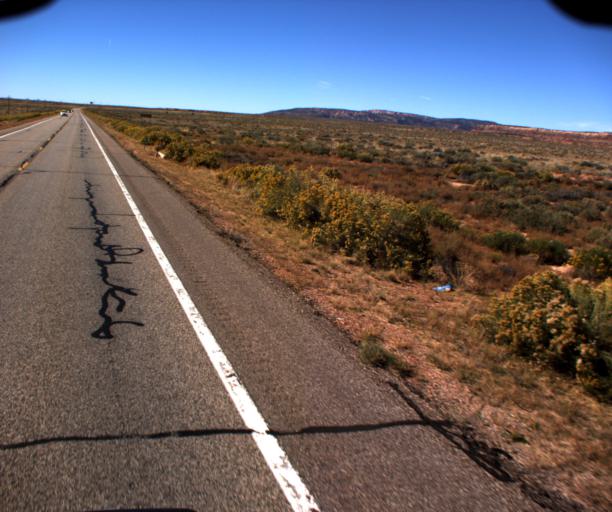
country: US
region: Arizona
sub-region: Coconino County
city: Fredonia
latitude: 36.8865
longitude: -112.6297
